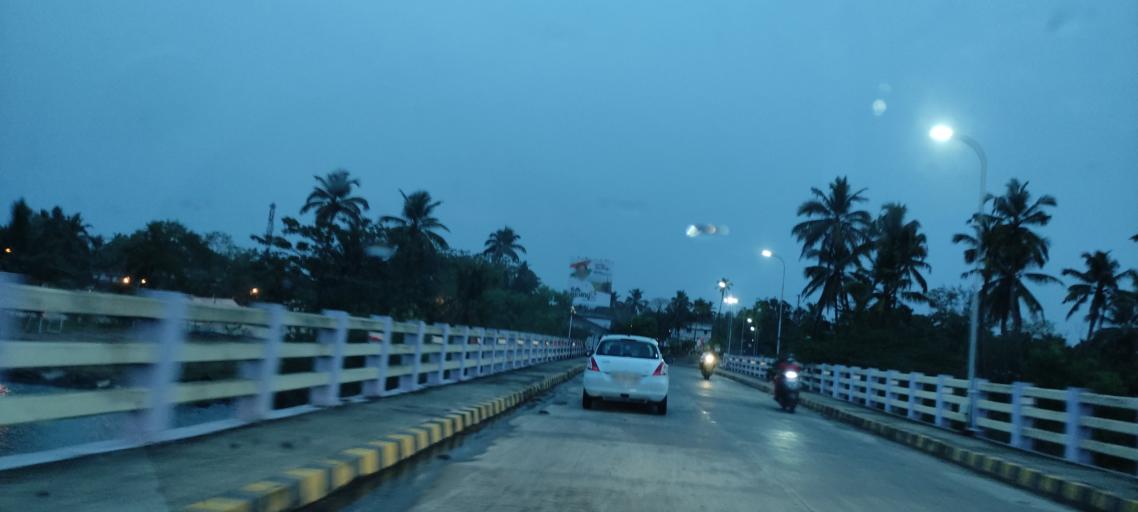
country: IN
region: Kerala
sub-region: Ernakulam
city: Cochin
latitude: 9.9222
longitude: 76.2875
